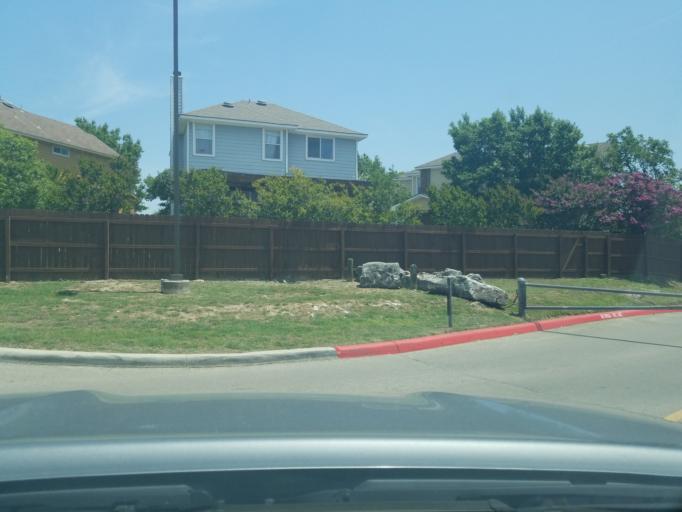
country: US
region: Texas
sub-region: Bexar County
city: Hollywood Park
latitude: 29.6436
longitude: -98.5181
